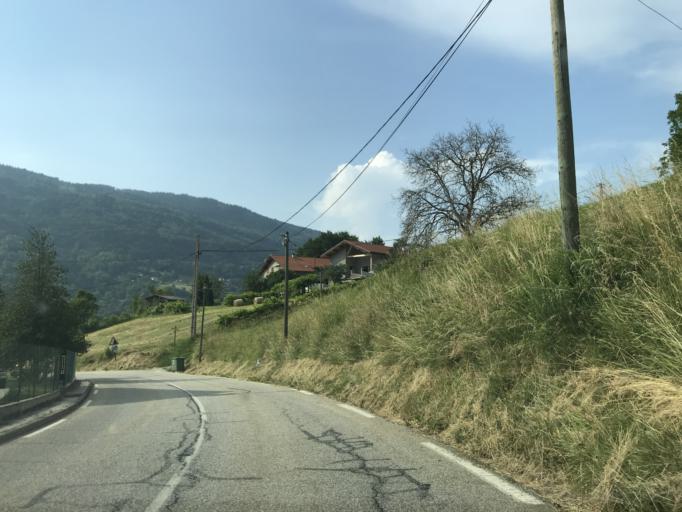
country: FR
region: Rhone-Alpes
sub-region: Departement de l'Isere
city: Allevard
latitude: 45.3938
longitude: 6.0799
